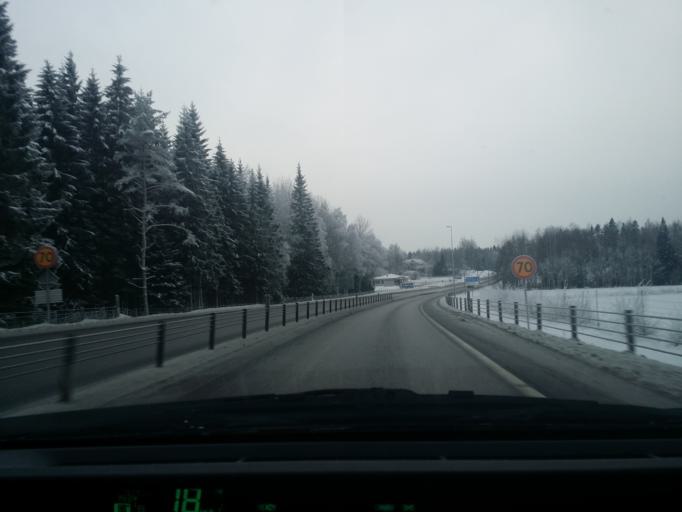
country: SE
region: Vaestra Goetaland
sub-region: Gullspangs Kommun
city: Anderstorp
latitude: 58.8849
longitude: 14.2993
